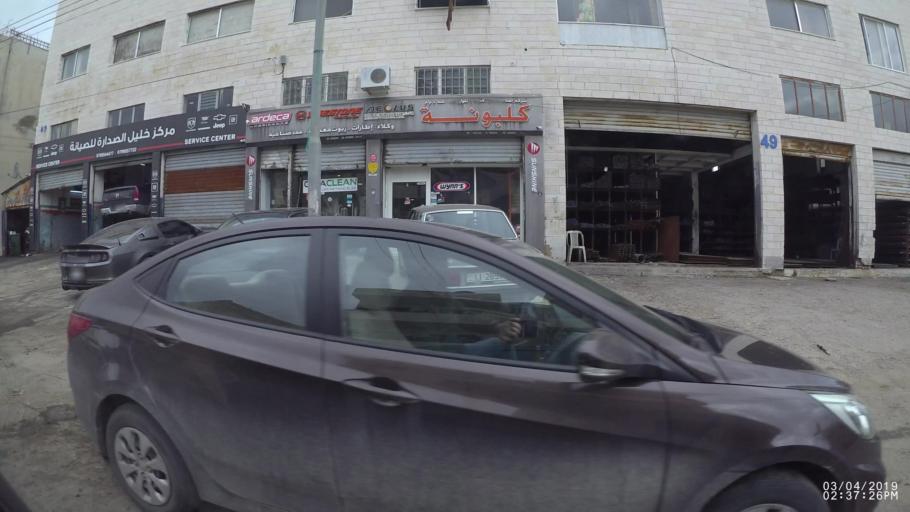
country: JO
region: Amman
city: Wadi as Sir
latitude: 31.9418
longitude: 35.8390
